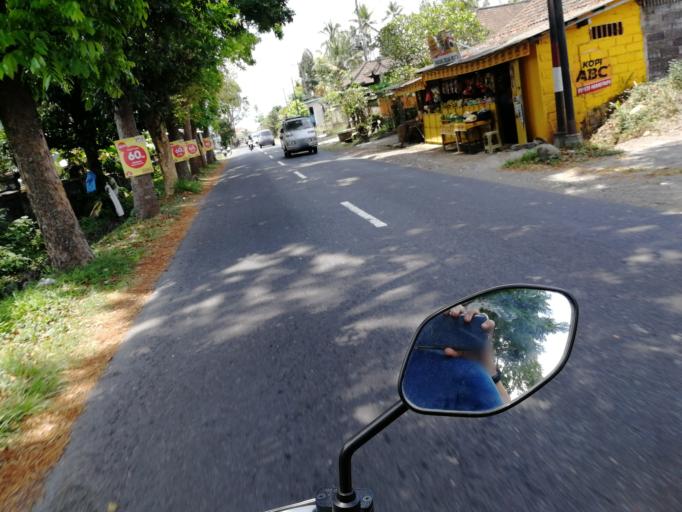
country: ID
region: Bali
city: Banjar Kubu
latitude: -8.4348
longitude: 115.4164
